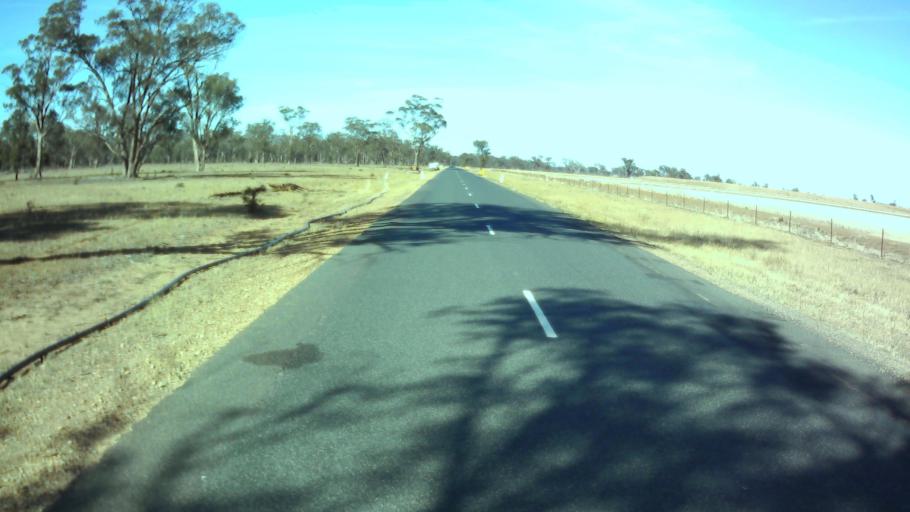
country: AU
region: New South Wales
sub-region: Weddin
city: Grenfell
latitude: -34.1265
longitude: 147.8023
